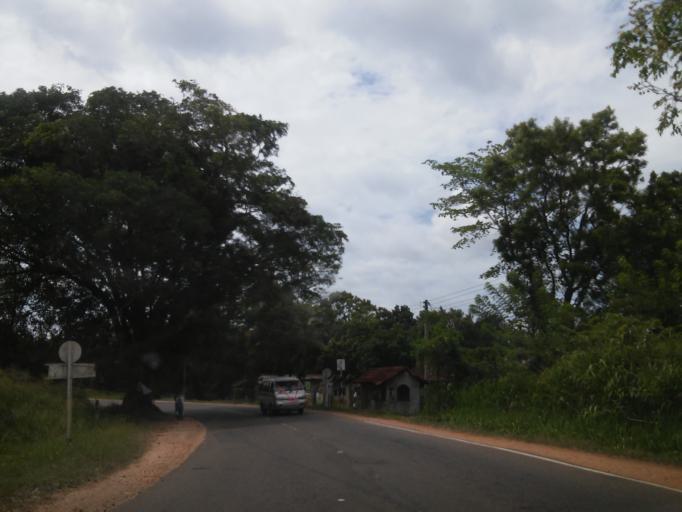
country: LK
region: Central
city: Sigiriya
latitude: 8.0590
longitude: 80.7139
